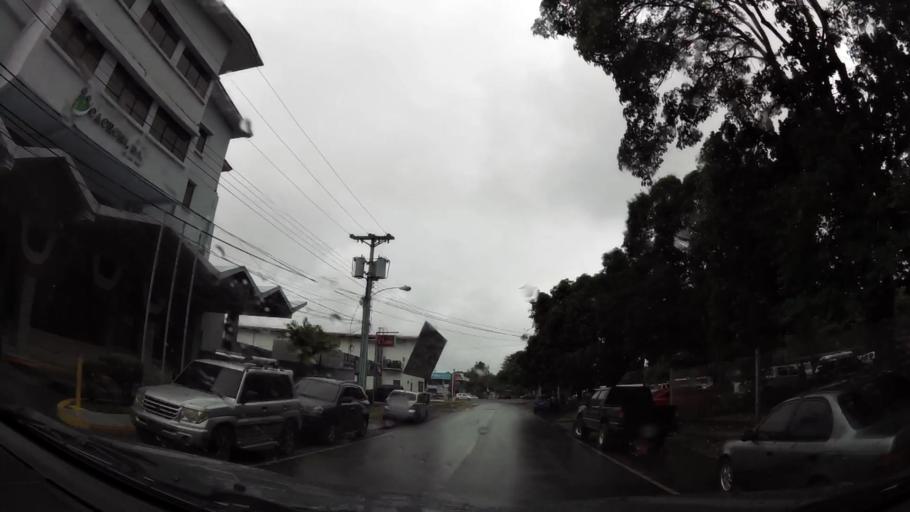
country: PA
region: Chiriqui
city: David
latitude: 8.4382
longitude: -82.4363
